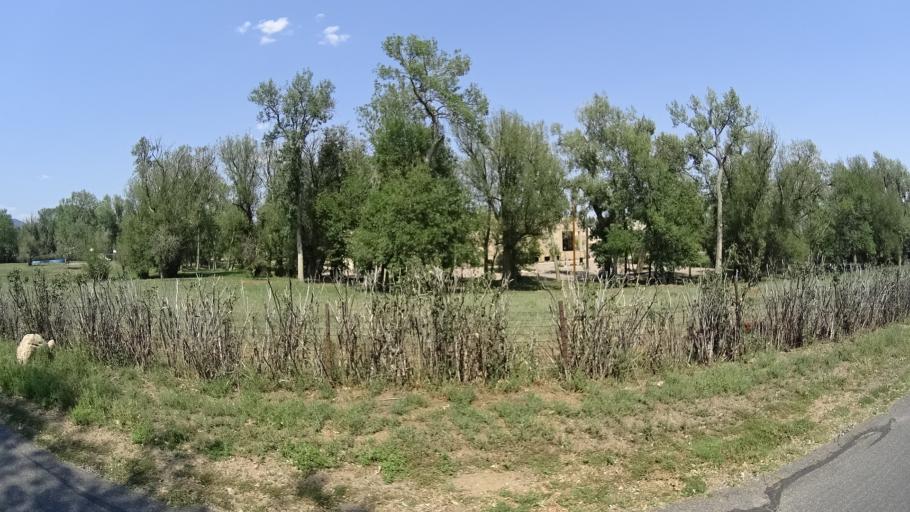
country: US
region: Colorado
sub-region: El Paso County
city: Colorado Springs
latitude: 38.7885
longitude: -104.8408
